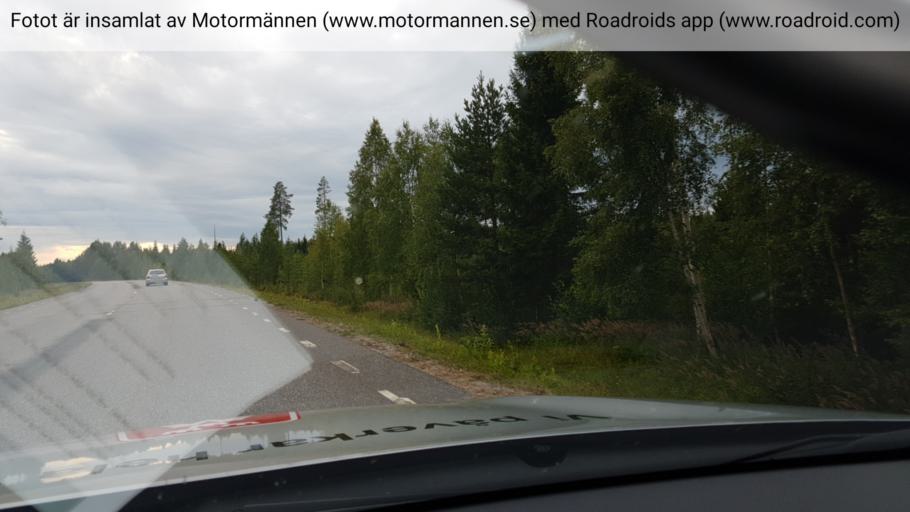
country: SE
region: Norrbotten
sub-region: Lulea Kommun
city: Gammelstad
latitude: 65.6625
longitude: 22.0679
